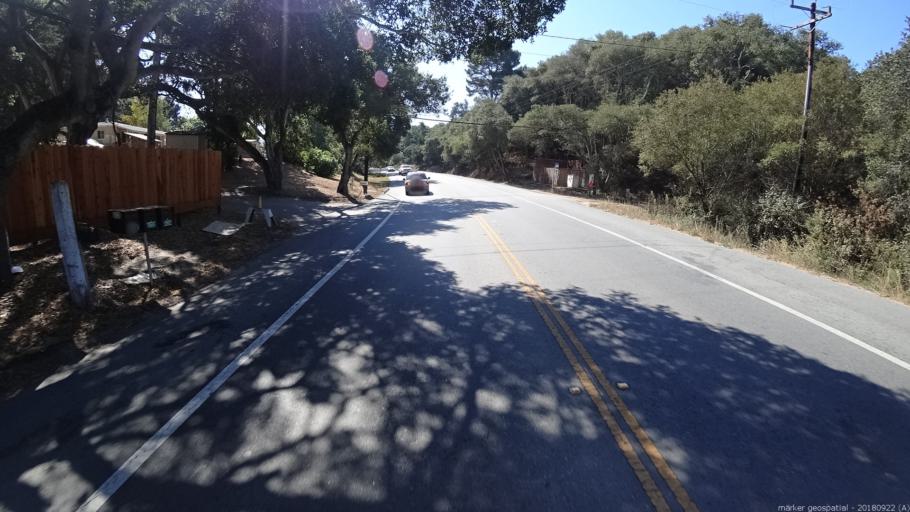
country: US
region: California
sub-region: Monterey County
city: Las Lomas
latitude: 36.8437
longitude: -121.6895
